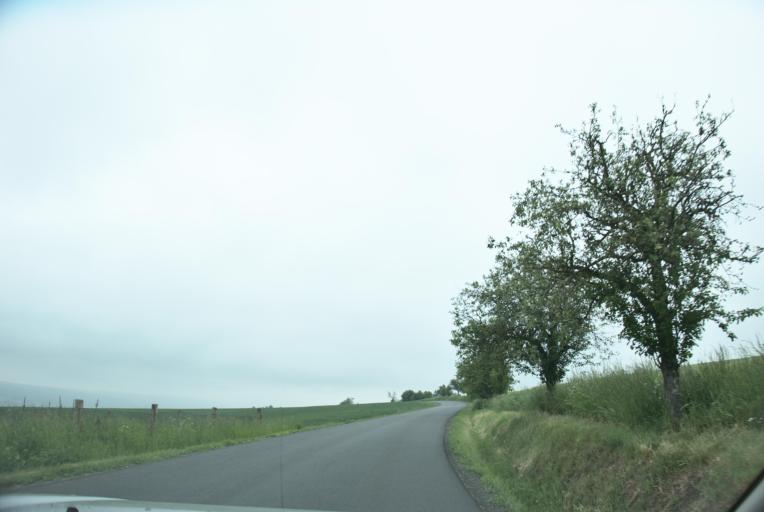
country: CZ
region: Plzensky
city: Zihle
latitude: 50.0195
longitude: 13.3962
